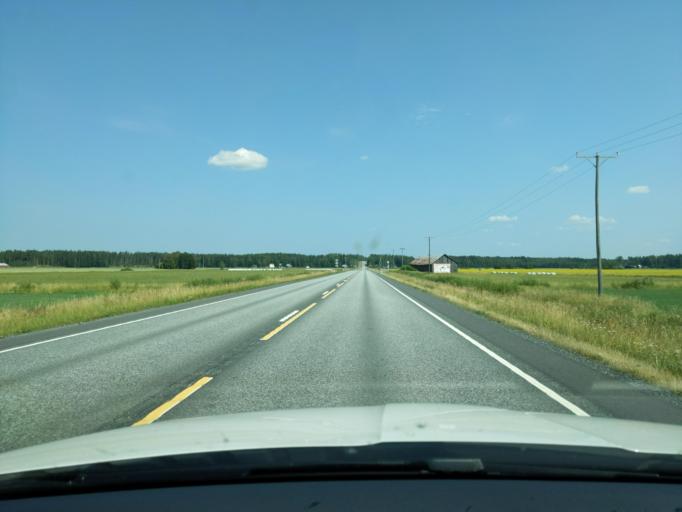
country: FI
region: Haeme
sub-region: Forssa
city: Ypaejae
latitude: 60.7569
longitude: 23.3056
